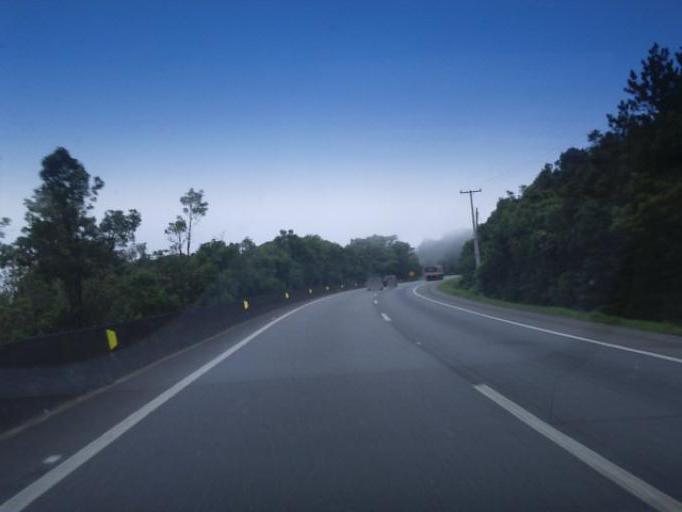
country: BR
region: Parana
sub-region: Sao Jose Dos Pinhais
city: Sao Jose dos Pinhais
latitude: -25.8459
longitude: -49.0360
